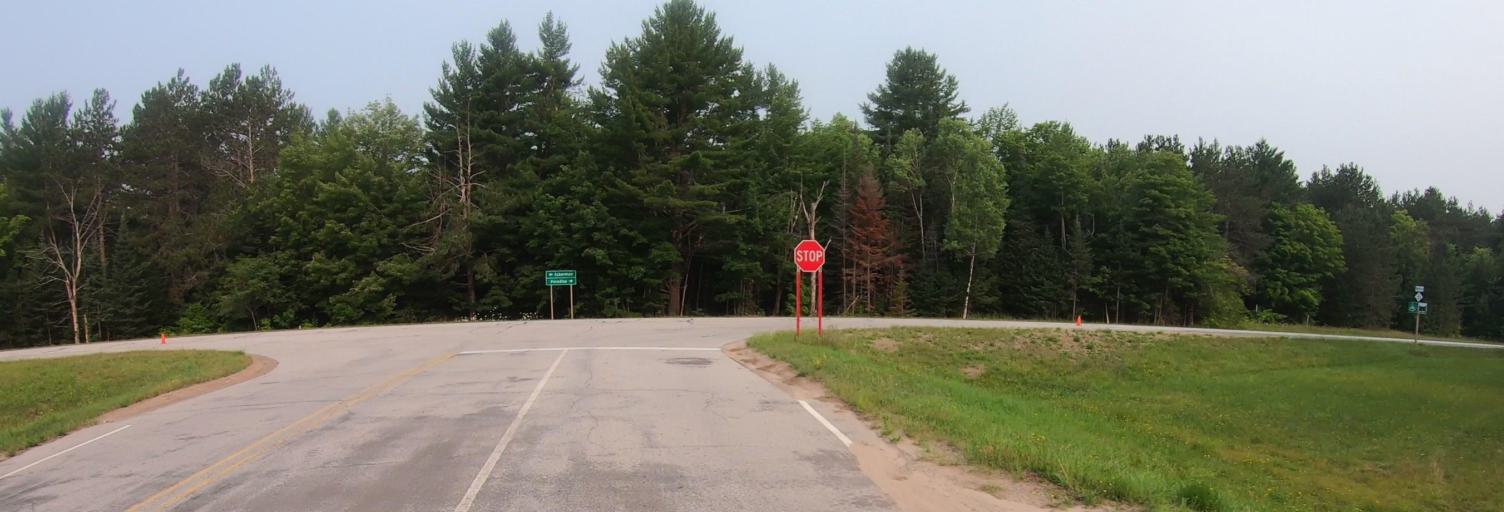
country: US
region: Michigan
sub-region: Luce County
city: Newberry
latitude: 46.4868
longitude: -85.1006
